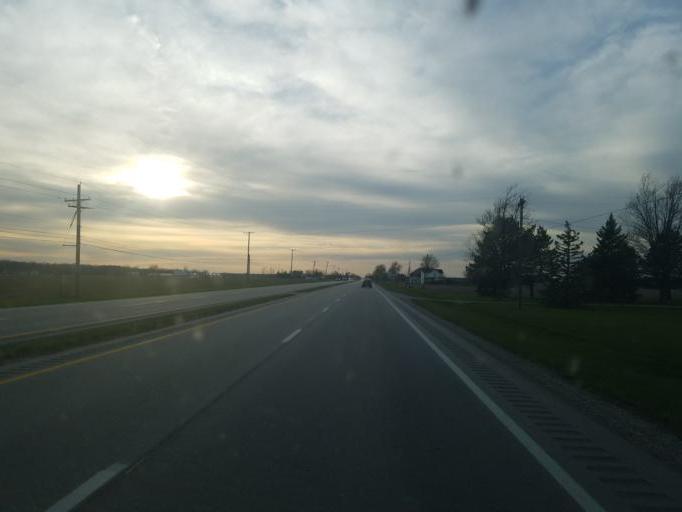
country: US
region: Ohio
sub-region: Sandusky County
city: Gibsonburg
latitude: 41.4125
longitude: -83.2690
